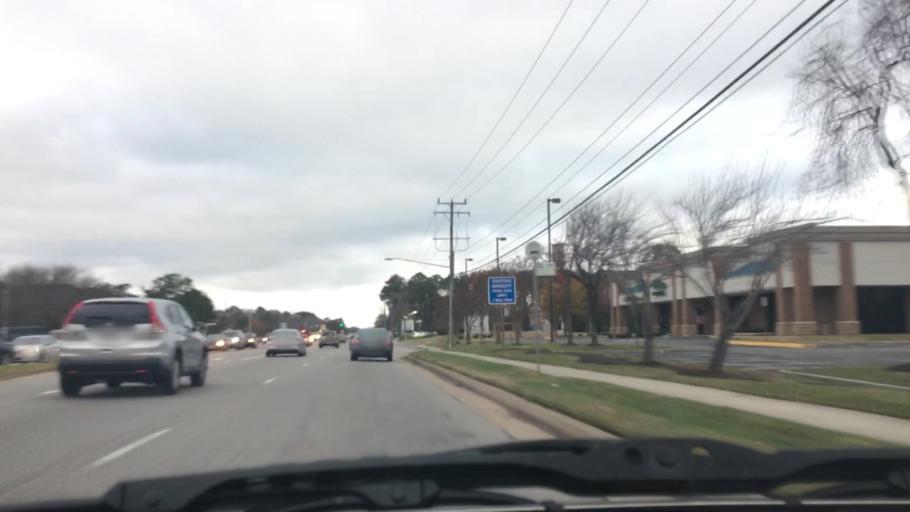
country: US
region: Virginia
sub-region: City of Virginia Beach
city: Virginia Beach
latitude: 36.8216
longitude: -76.1235
